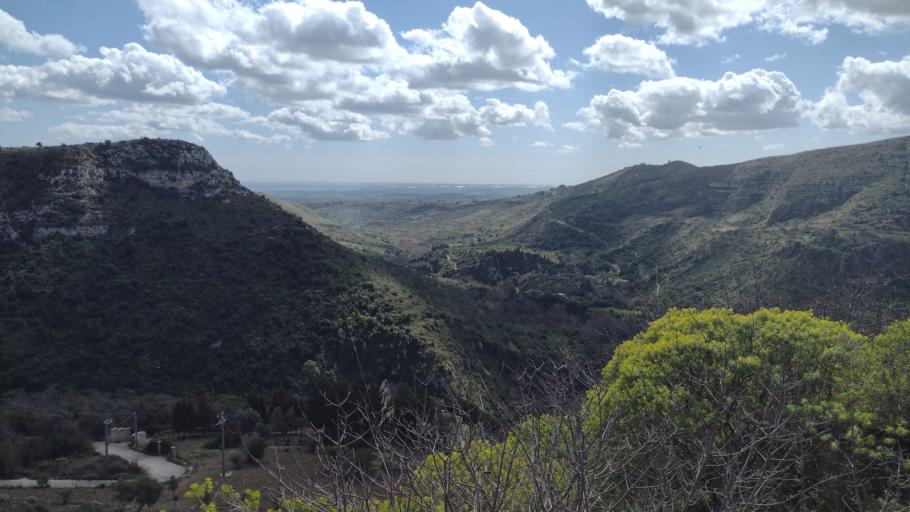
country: IT
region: Sicily
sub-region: Provincia di Siracusa
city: Noto
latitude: 36.9327
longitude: 15.0252
